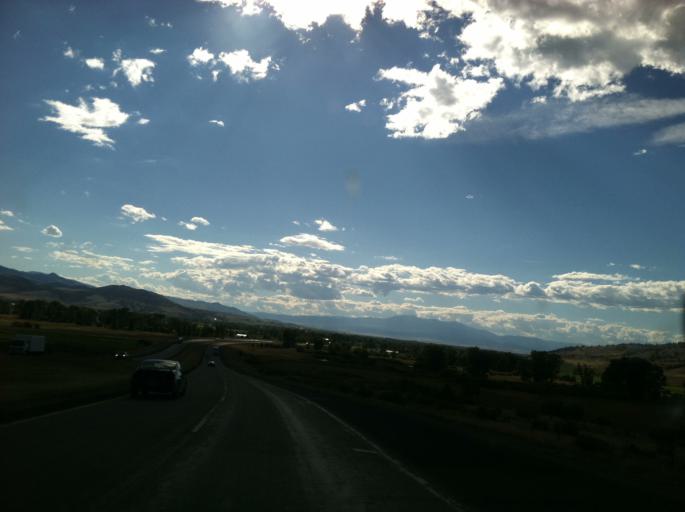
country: US
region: Montana
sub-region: Jefferson County
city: Whitehall
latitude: 45.8756
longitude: -111.9298
